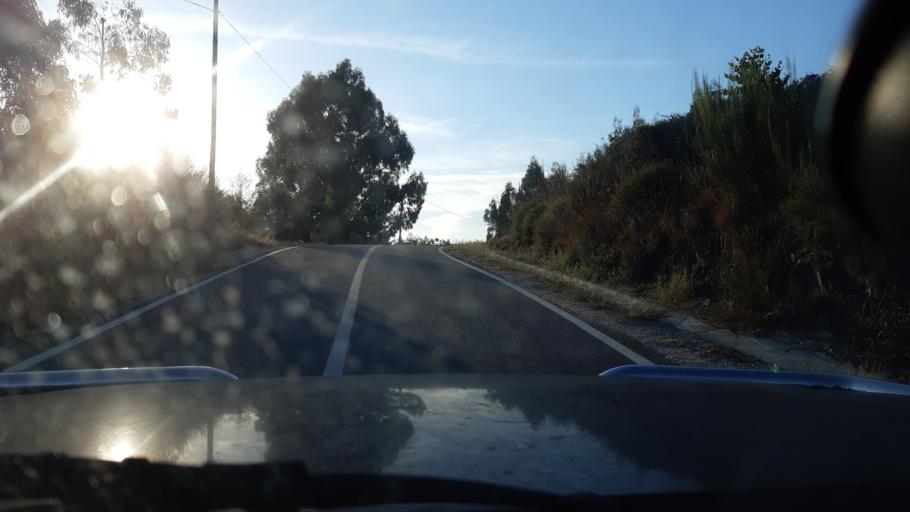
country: PT
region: Viseu
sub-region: Mortagua
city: Mortagua
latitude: 40.5408
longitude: -8.2501
